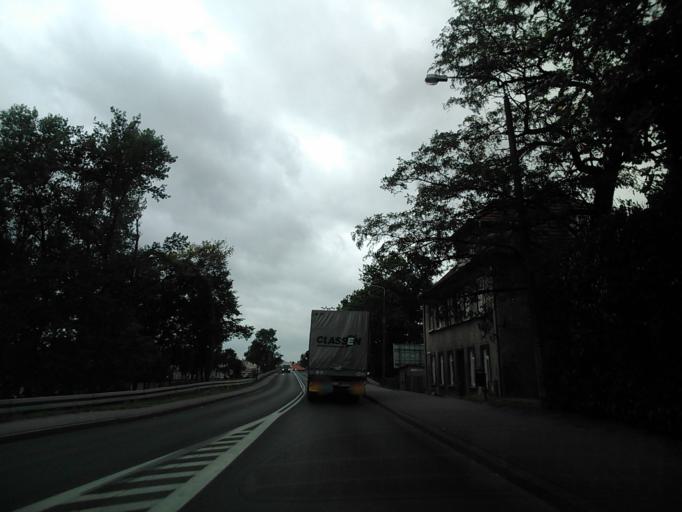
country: PL
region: Kujawsko-Pomorskie
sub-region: Powiat inowroclawski
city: Kruszwica
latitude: 52.6743
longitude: 18.3304
